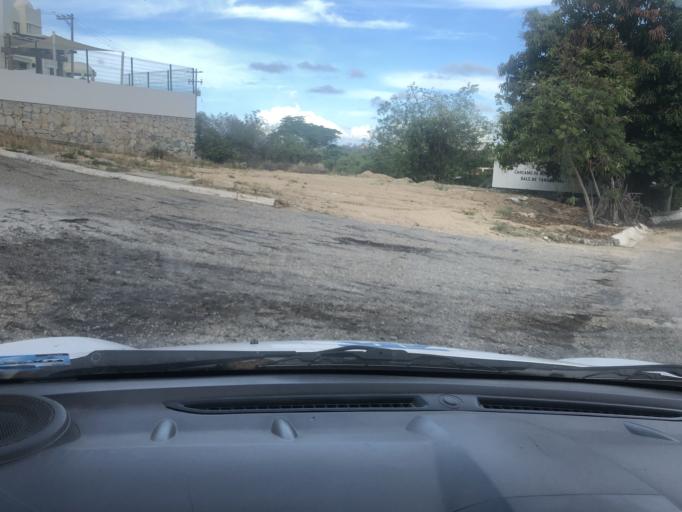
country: MX
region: Oaxaca
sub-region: Santa Maria Huatulco
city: Crucecita
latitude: 15.7714
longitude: -96.0870
